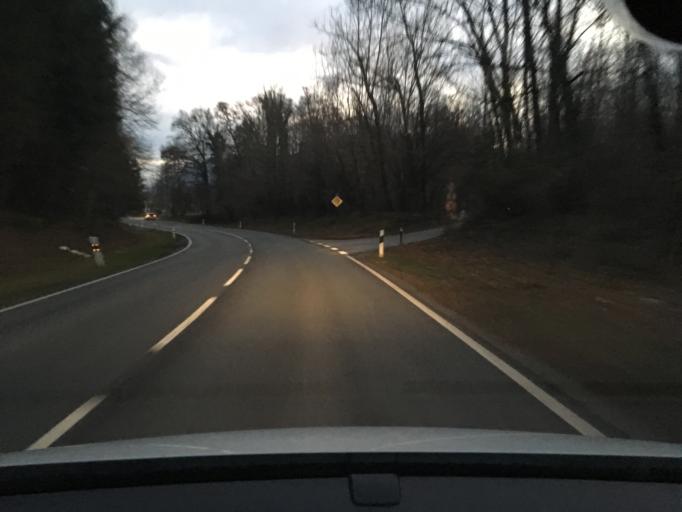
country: DE
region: Bavaria
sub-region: Upper Bavaria
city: Brannenburg
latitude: 47.7603
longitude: 12.1052
